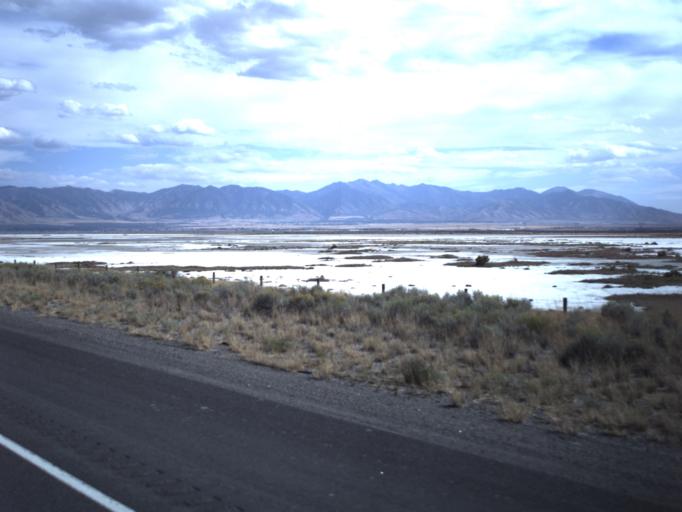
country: US
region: Utah
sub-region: Tooele County
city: Grantsville
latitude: 40.6822
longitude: -112.4320
